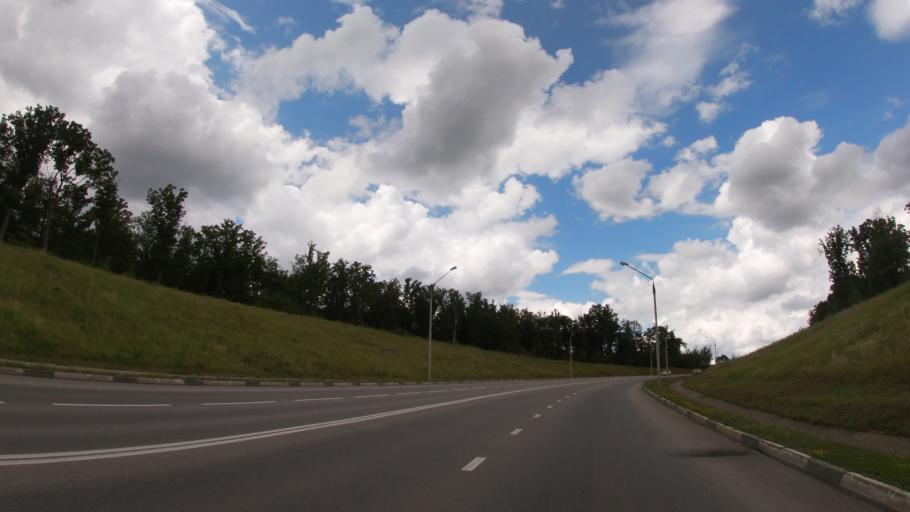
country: RU
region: Belgorod
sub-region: Belgorodskiy Rayon
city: Belgorod
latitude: 50.6231
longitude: 36.6121
